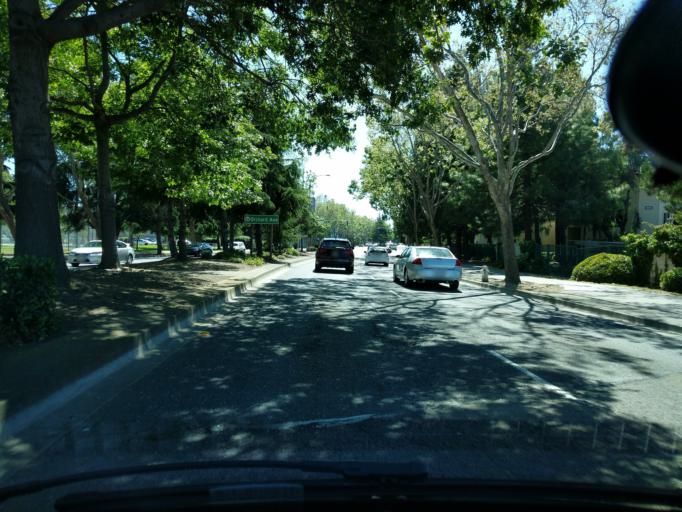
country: US
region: California
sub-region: Alameda County
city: San Leandro
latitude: 37.7227
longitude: -122.1644
